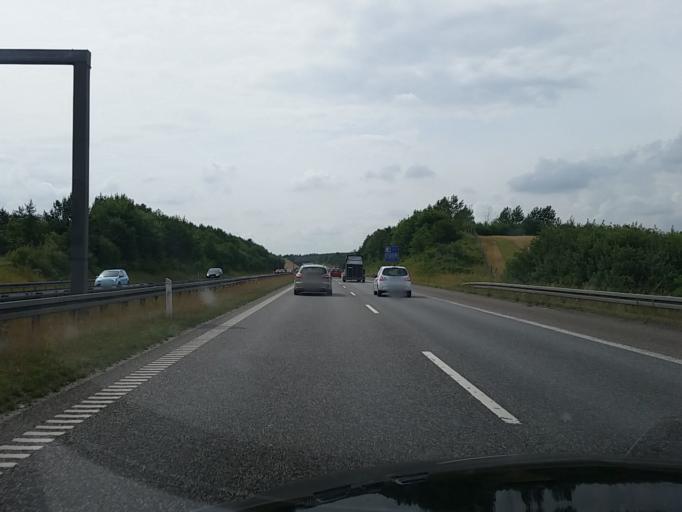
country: DK
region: South Denmark
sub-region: Kolding Kommune
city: Kolding
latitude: 55.5145
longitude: 9.4201
